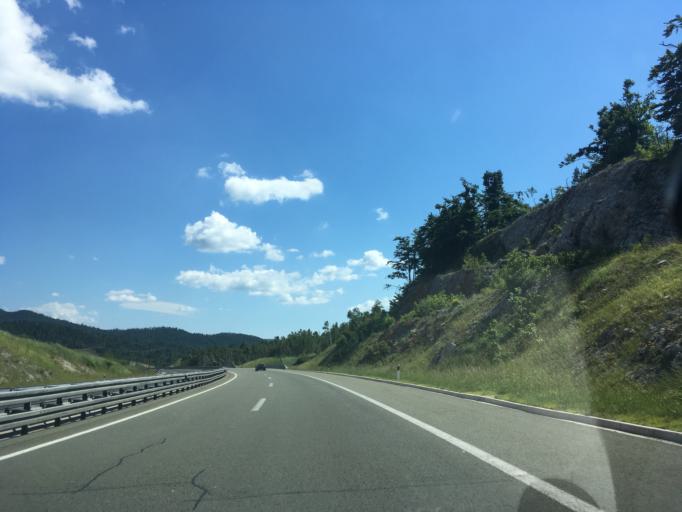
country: HR
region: Primorsko-Goranska
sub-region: Grad Delnice
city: Delnice
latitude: 45.3340
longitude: 14.7383
